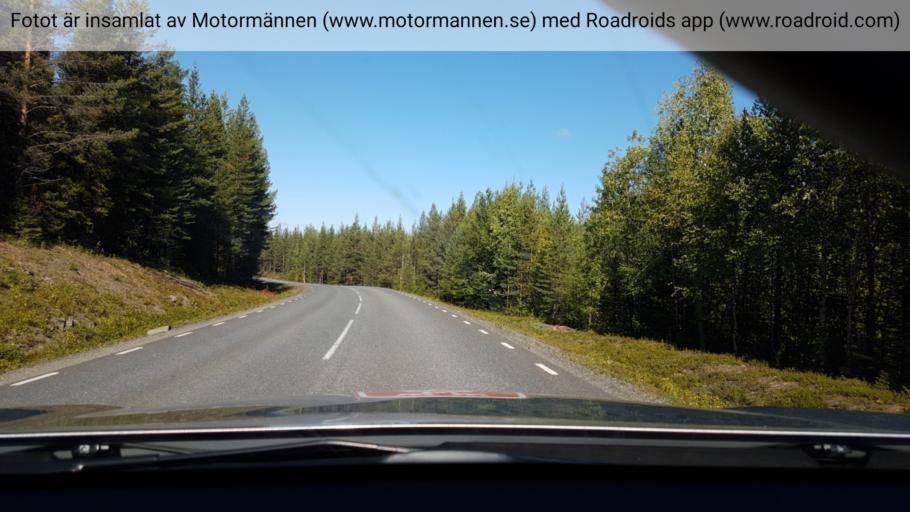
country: SE
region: Vaesterbotten
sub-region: Norsjo Kommun
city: Norsjoe
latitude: 64.9949
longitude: 19.4300
